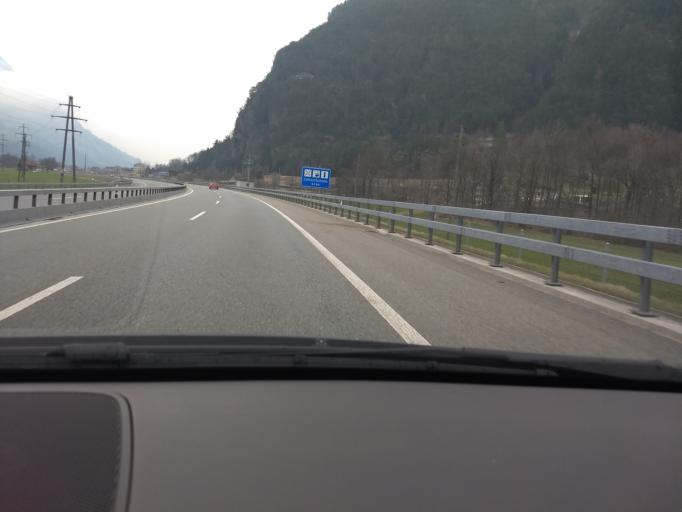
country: CH
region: Uri
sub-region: Uri
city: Erstfeld
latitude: 46.8082
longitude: 8.6604
